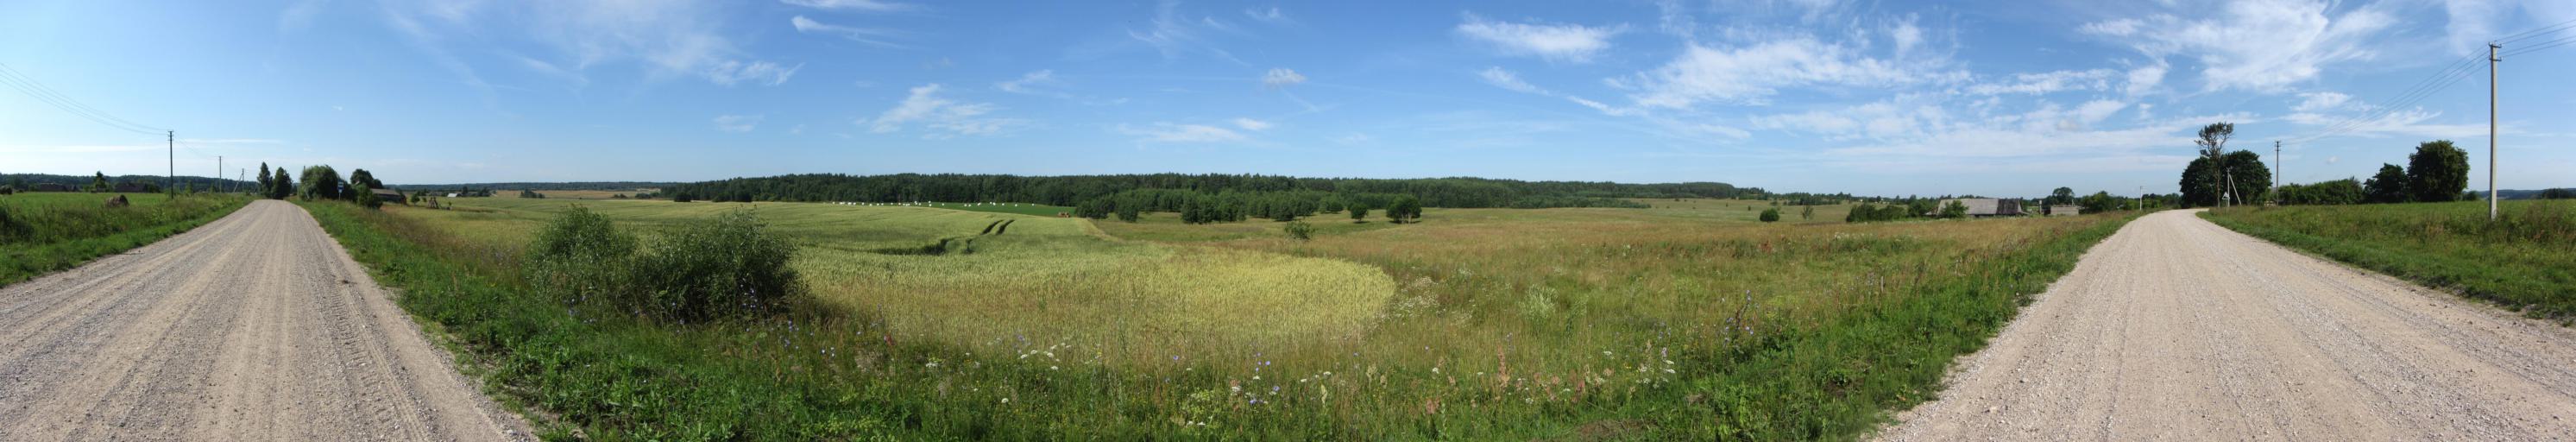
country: LT
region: Vilnius County
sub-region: Vilniaus Rajonas
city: Vievis
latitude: 54.8523
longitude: 24.8351
